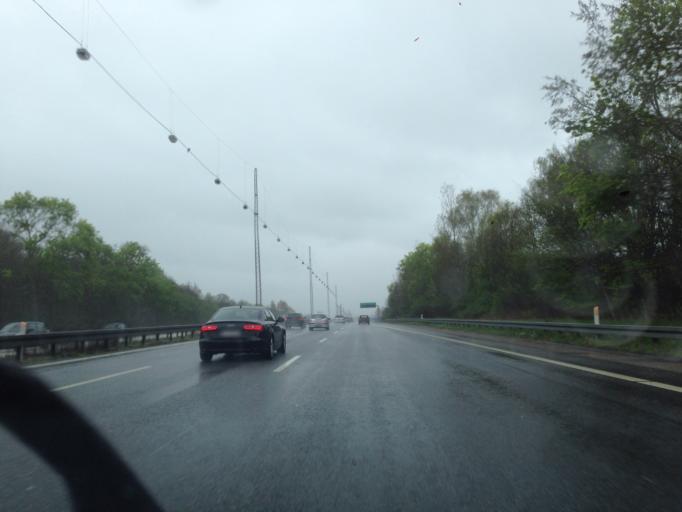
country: DK
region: Capital Region
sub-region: Lyngby-Tarbaek Kommune
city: Kongens Lyngby
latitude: 55.7823
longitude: 12.5268
